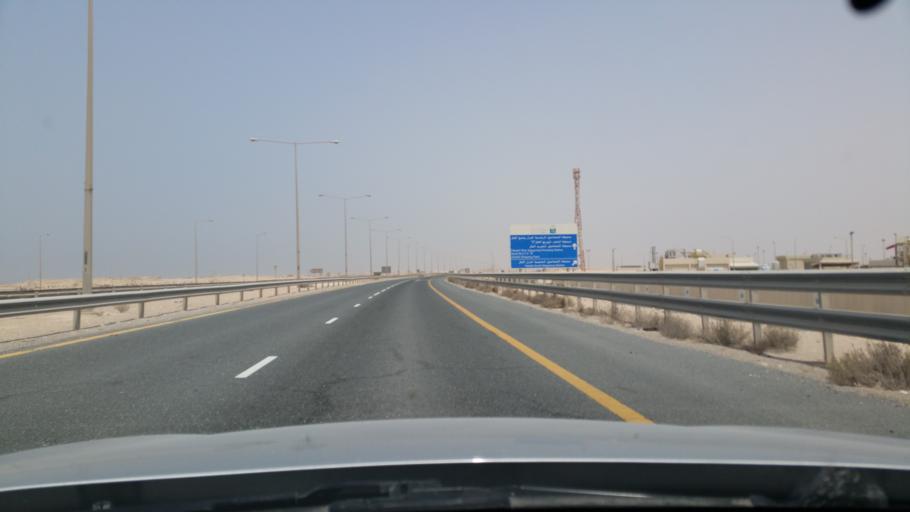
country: QA
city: Umm Bab
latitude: 25.2312
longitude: 50.8026
